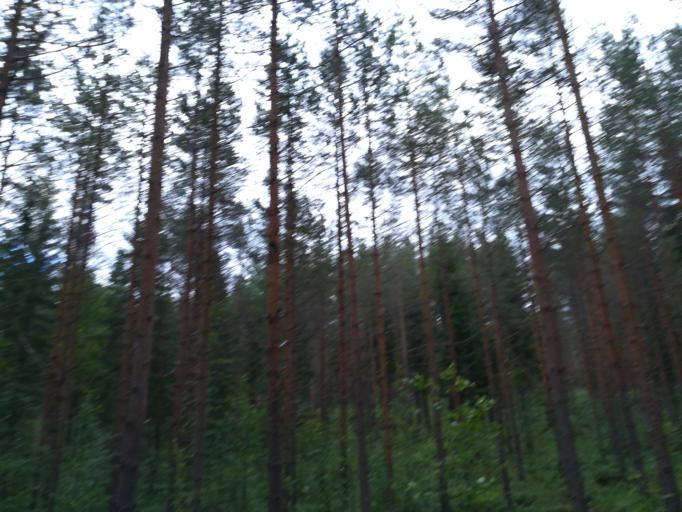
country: FI
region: South Karelia
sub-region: Lappeenranta
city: Savitaipale
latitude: 61.3036
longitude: 27.6172
